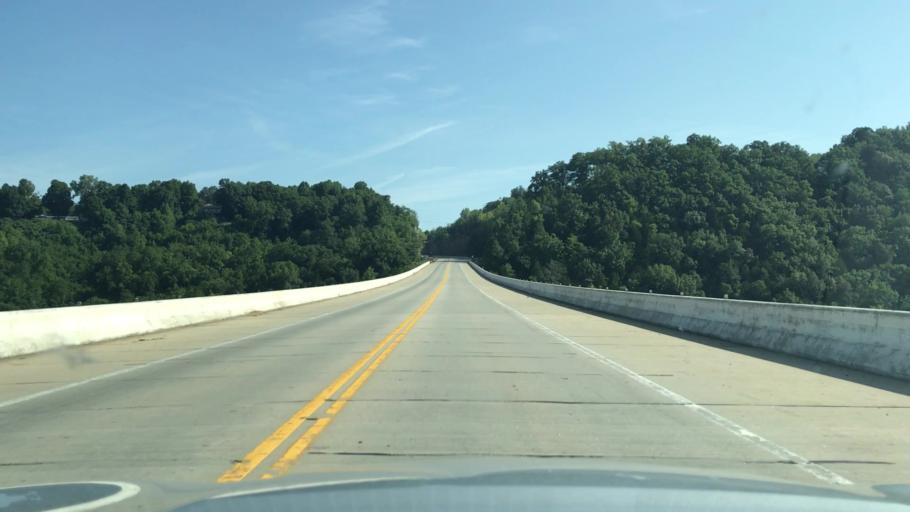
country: US
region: Tennessee
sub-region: Pickett County
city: Byrdstown
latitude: 36.5328
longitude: -85.1611
